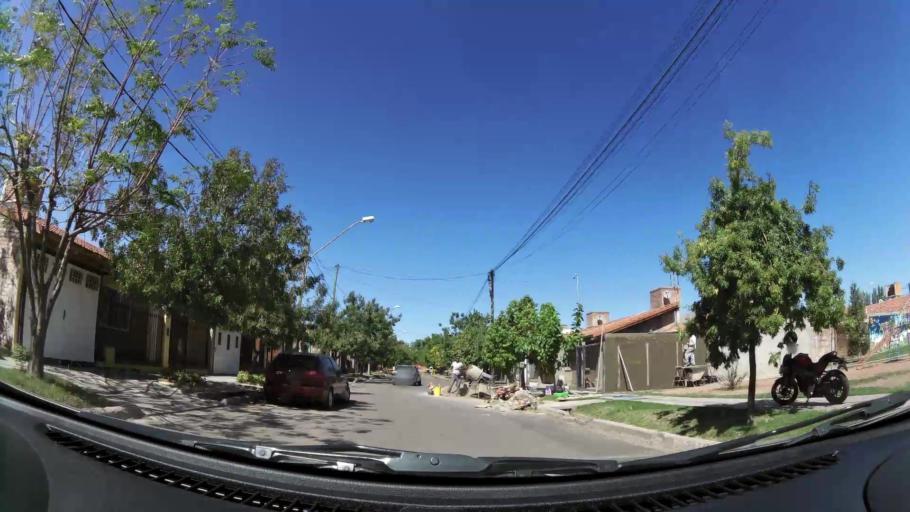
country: AR
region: Mendoza
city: Villa Nueva
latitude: -32.9006
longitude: -68.7752
